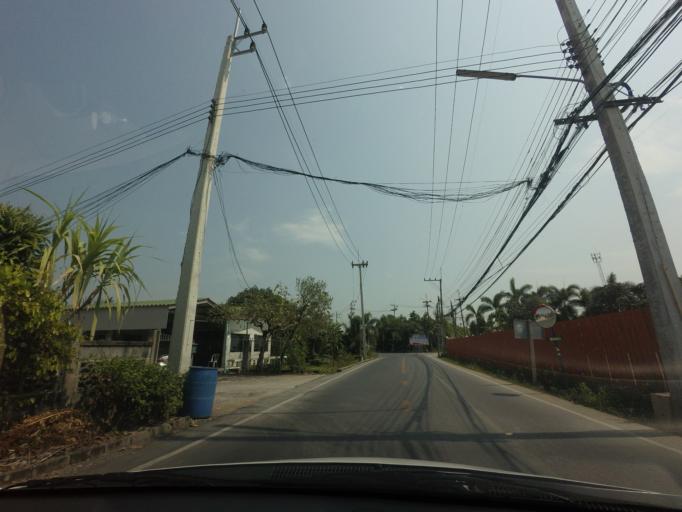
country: TH
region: Samut Sakhon
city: Krathum Baen
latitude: 13.6934
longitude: 100.2529
